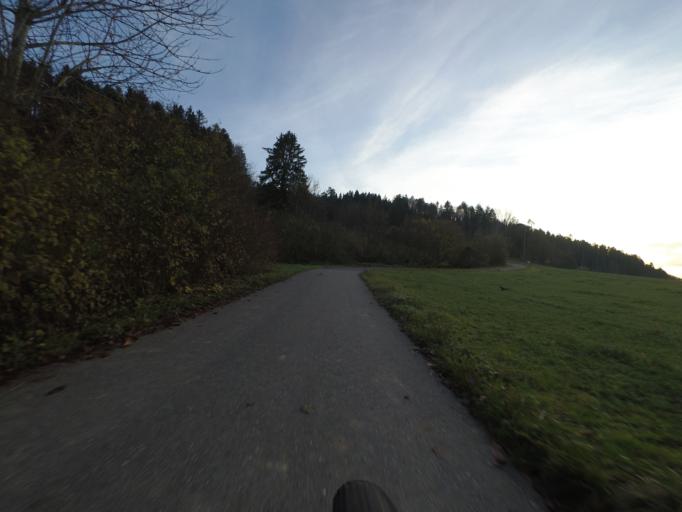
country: CH
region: Thurgau
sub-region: Frauenfeld District
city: Pfyn
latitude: 47.5747
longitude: 8.9617
